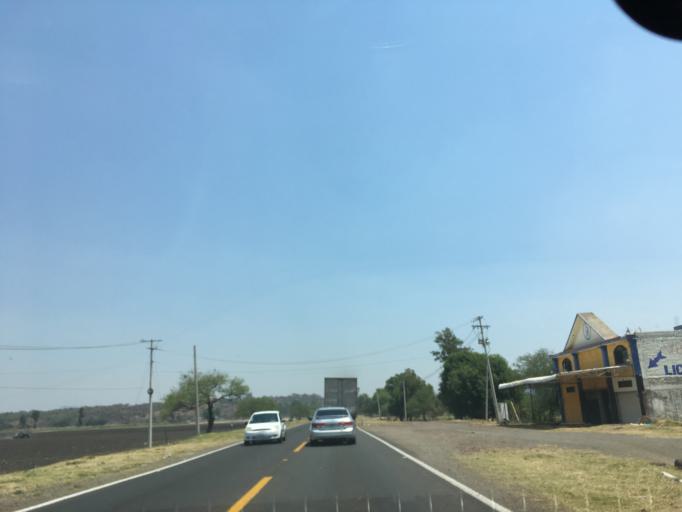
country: MX
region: Michoacan
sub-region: Cuitzeo
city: Cuamio
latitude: 20.0731
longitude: -101.1557
